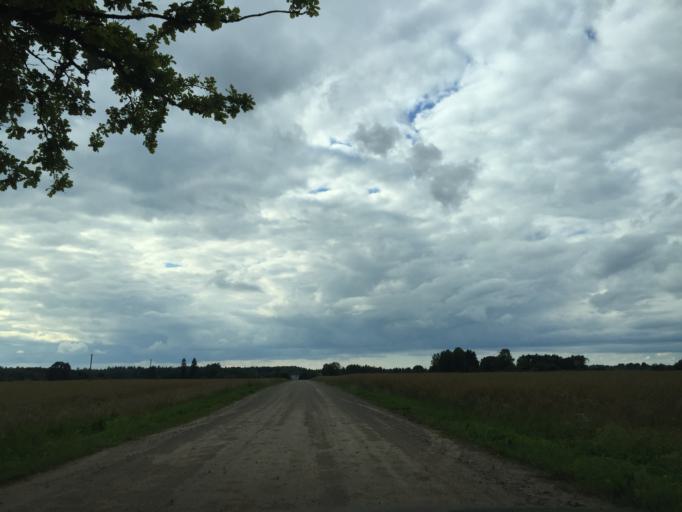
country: LV
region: Malpils
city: Malpils
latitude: 56.9478
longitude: 24.9965
